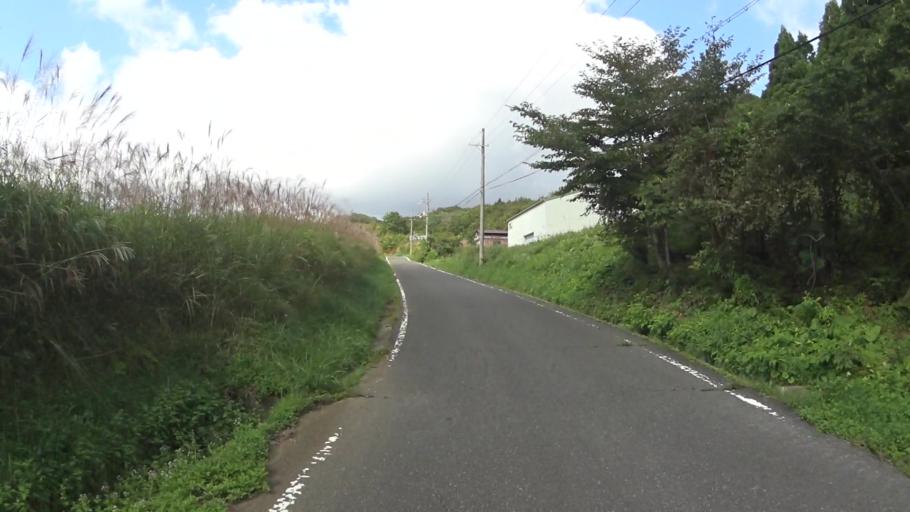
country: JP
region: Kyoto
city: Miyazu
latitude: 35.6556
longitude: 135.1830
